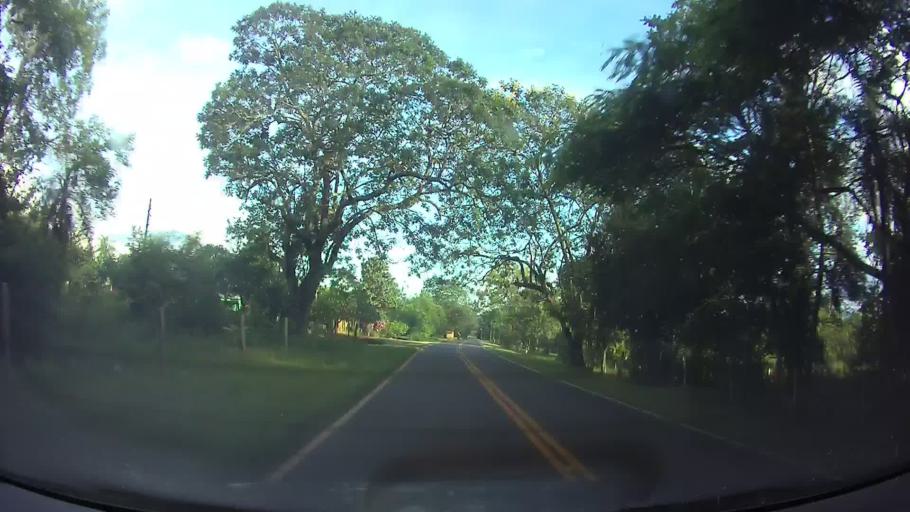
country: PY
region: Paraguari
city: Ybycui
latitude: -25.9662
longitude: -57.0828
